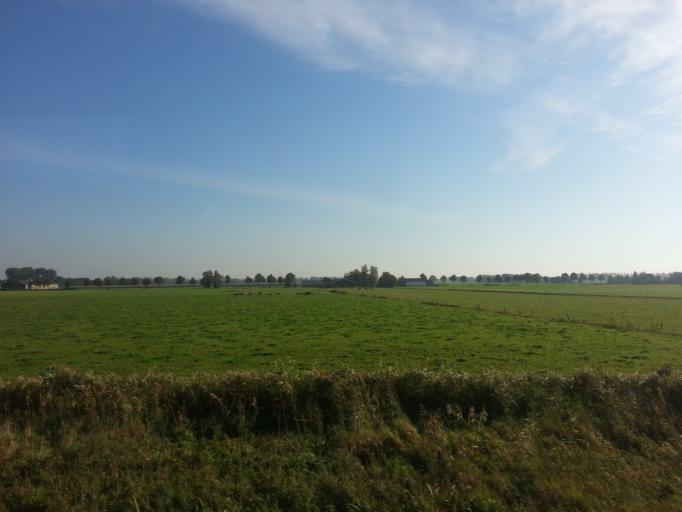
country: NL
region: Gelderland
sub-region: Gemeente Maasdriel
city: Hedel
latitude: 51.7801
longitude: 5.2688
